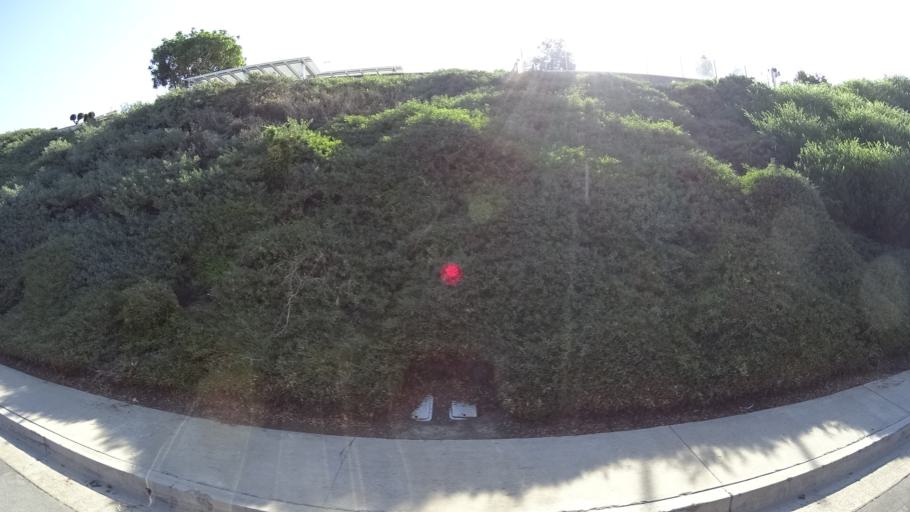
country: US
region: California
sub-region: Orange County
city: San Clemente
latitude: 33.4371
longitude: -117.6126
